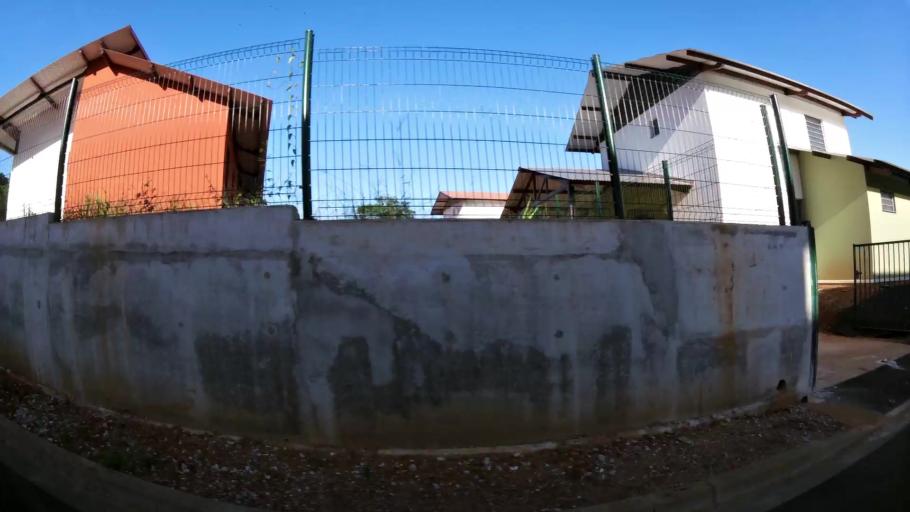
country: GF
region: Guyane
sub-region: Guyane
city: Remire-Montjoly
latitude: 4.8870
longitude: -52.2981
